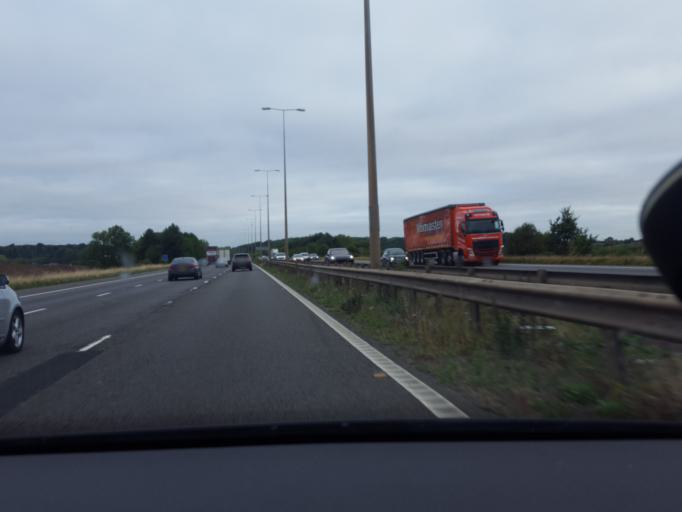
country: GB
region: England
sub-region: Leicestershire
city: Shepshed
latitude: 52.7771
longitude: -1.2793
